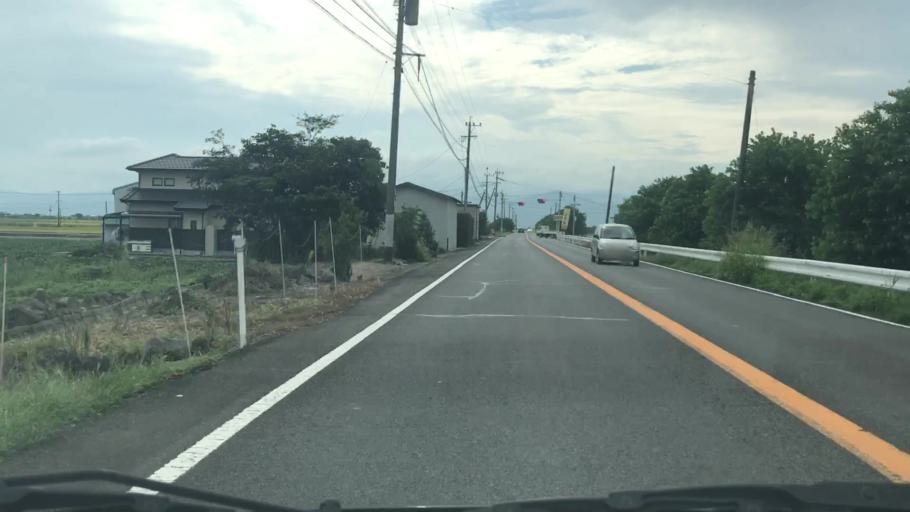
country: JP
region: Saga Prefecture
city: Kashima
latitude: 33.1448
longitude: 130.1472
